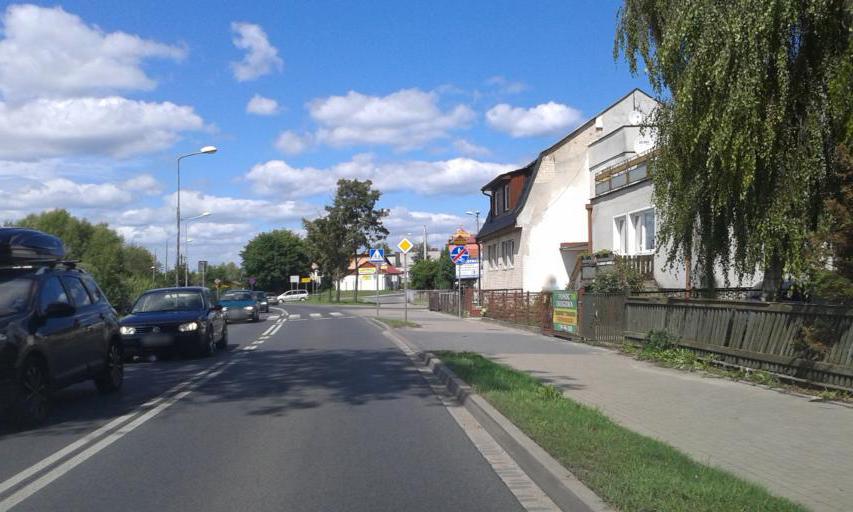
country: PL
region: West Pomeranian Voivodeship
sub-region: Powiat walecki
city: Walcz
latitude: 53.2790
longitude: 16.4638
